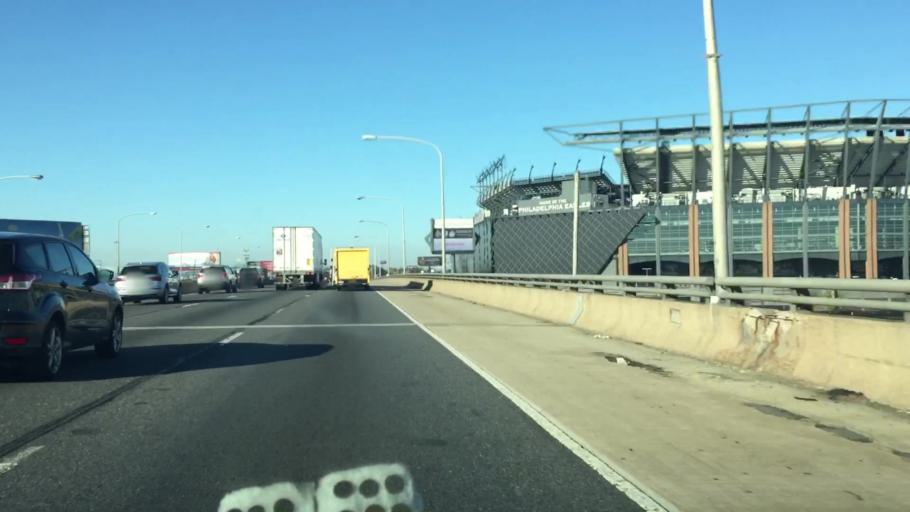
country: US
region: New Jersey
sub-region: Gloucester County
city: National Park
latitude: 39.8997
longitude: -75.1633
